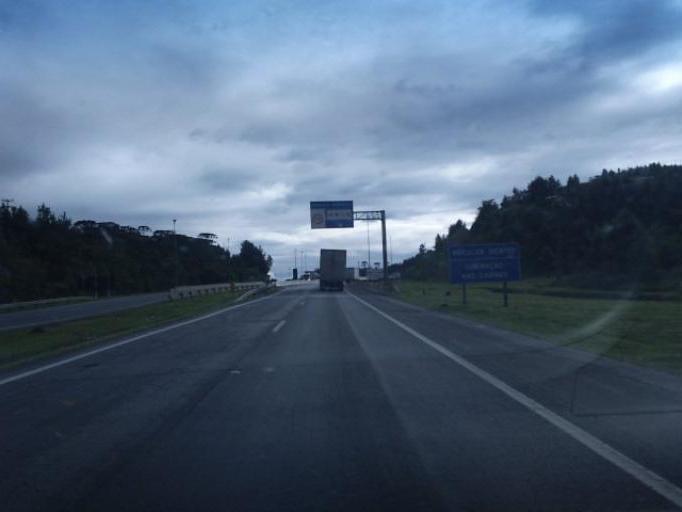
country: BR
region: Parana
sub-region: Campina Grande Do Sul
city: Campina Grande do Sul
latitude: -25.2863
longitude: -48.9313
